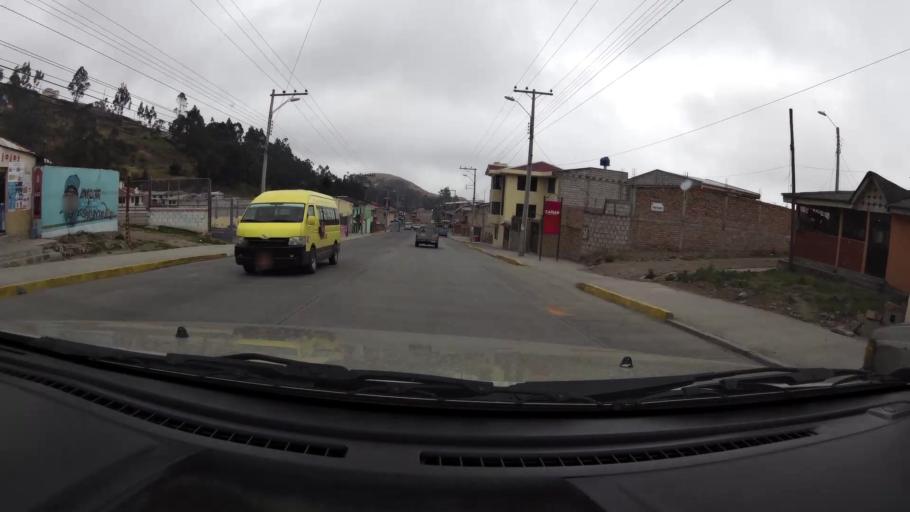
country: EC
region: Canar
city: Canar
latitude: -2.5633
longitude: -78.9420
